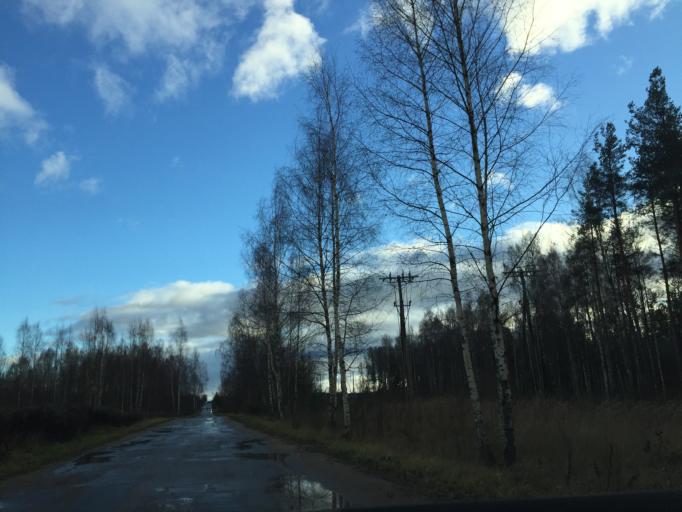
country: LV
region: Koceni
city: Koceni
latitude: 57.5374
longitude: 25.3787
